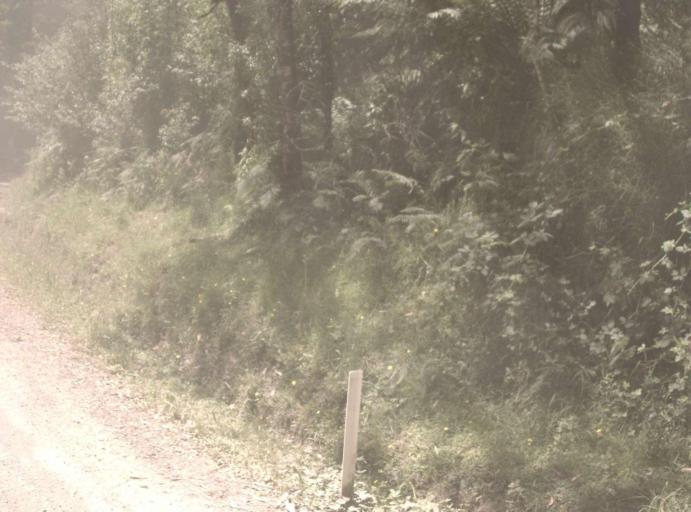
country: AU
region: Victoria
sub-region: Yarra Ranges
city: Millgrove
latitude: -37.6537
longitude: 145.7299
